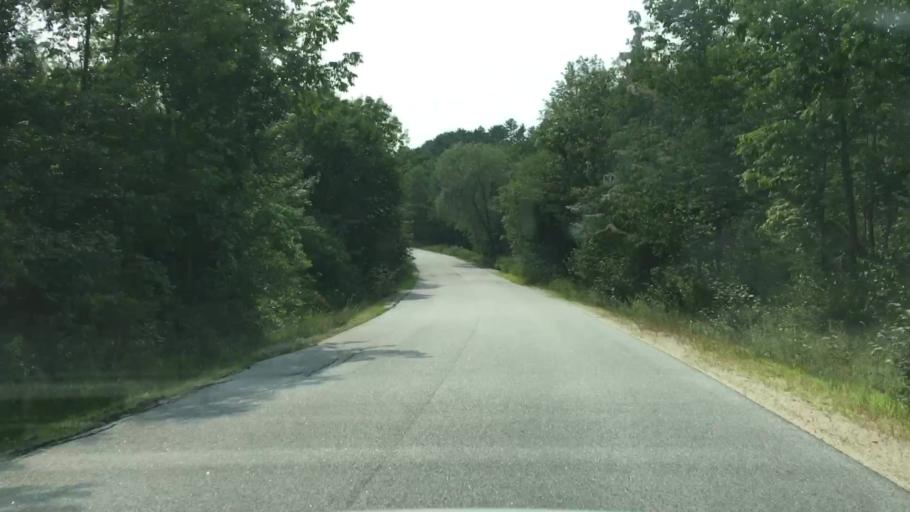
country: US
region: Maine
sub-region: Oxford County
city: Buckfield
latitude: 44.3007
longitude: -70.3099
